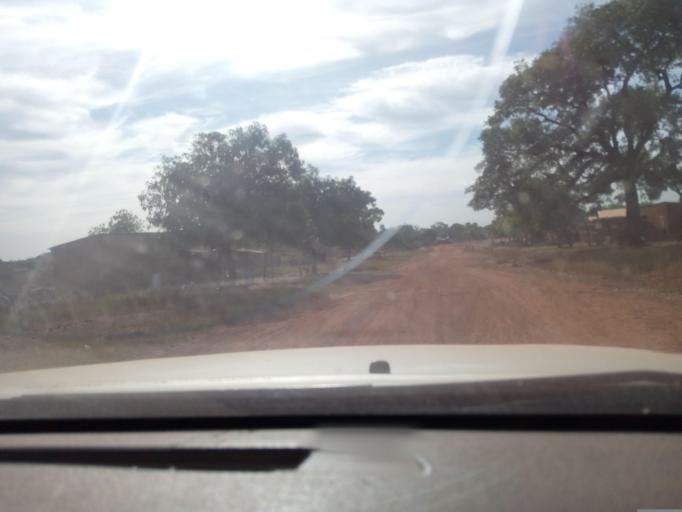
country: ML
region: Sikasso
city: Sikasso
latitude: 11.9017
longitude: -6.0537
